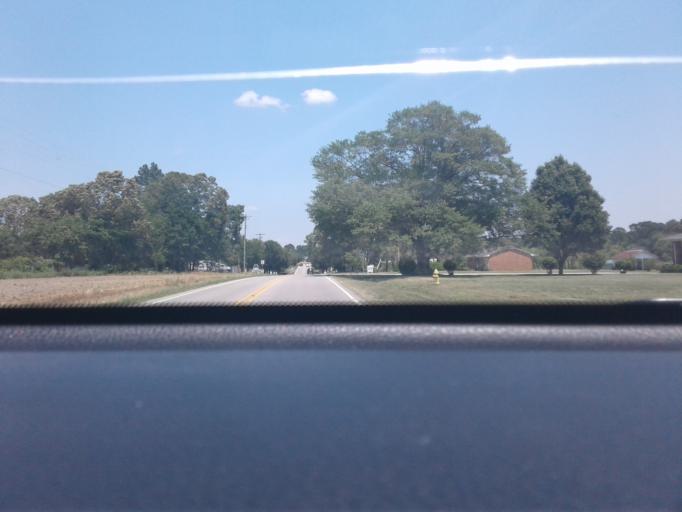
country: US
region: North Carolina
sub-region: Harnett County
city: Dunn
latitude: 35.3372
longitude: -78.5885
